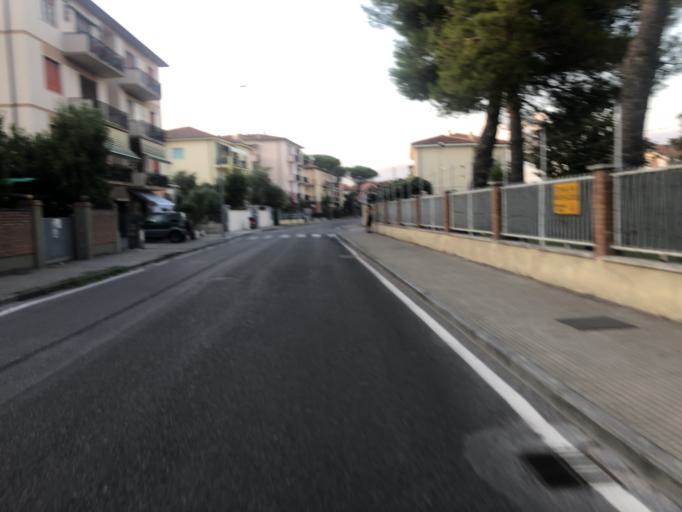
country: IT
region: Tuscany
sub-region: Province of Pisa
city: Pisa
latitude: 43.7306
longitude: 10.4072
